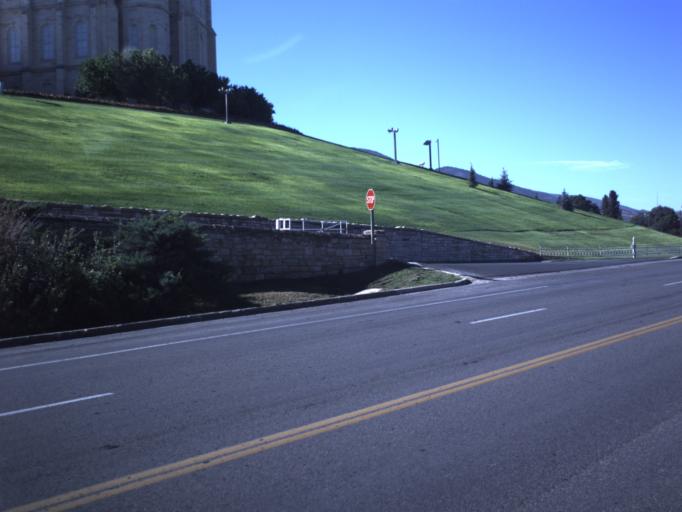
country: US
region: Utah
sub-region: Sanpete County
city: Manti
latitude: 39.2740
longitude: -111.6346
